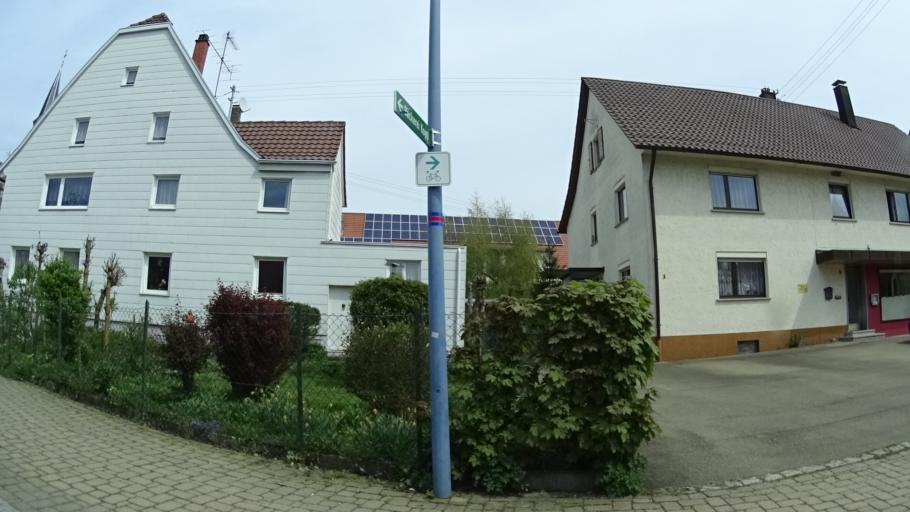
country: DE
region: Baden-Wuerttemberg
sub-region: Freiburg Region
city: Deisslingen
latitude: 48.1122
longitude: 8.6036
